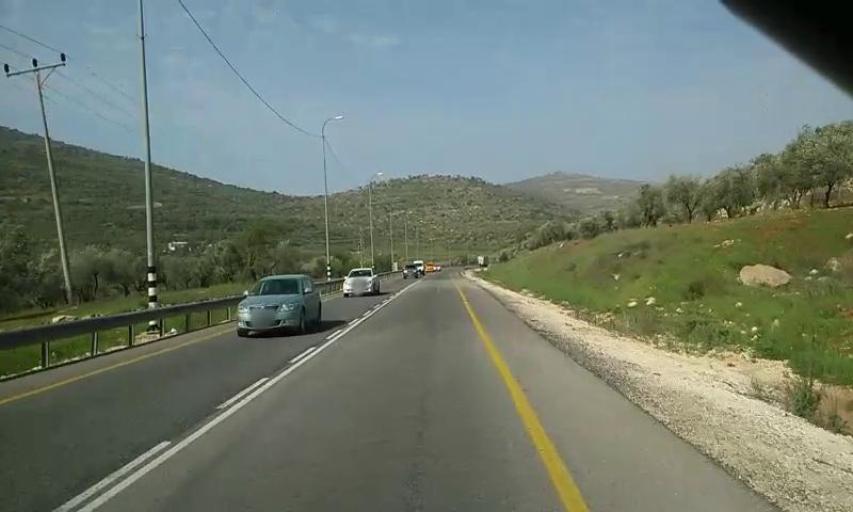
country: PS
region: West Bank
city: Al Lubban ash Sharqiyah
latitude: 32.0650
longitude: 35.2481
